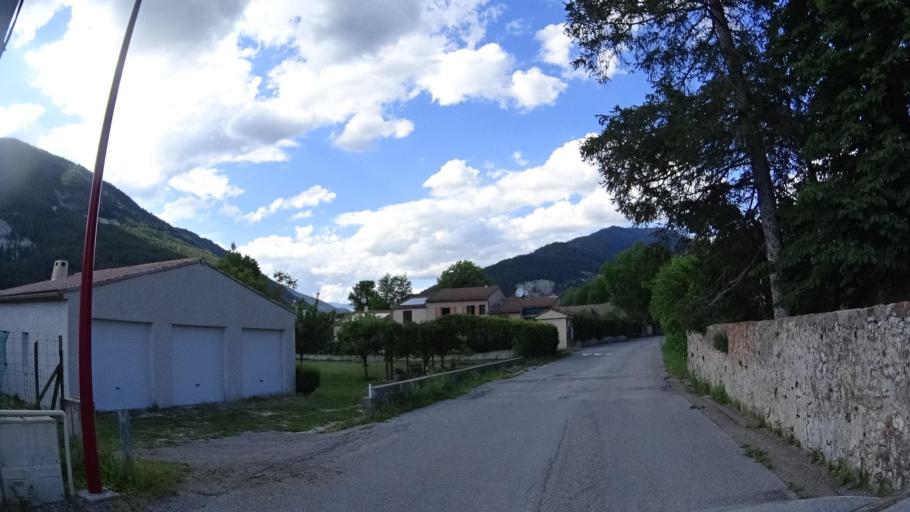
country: FR
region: Provence-Alpes-Cote d'Azur
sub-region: Departement des Alpes-de-Haute-Provence
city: Castellane
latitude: 43.9687
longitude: 6.5131
